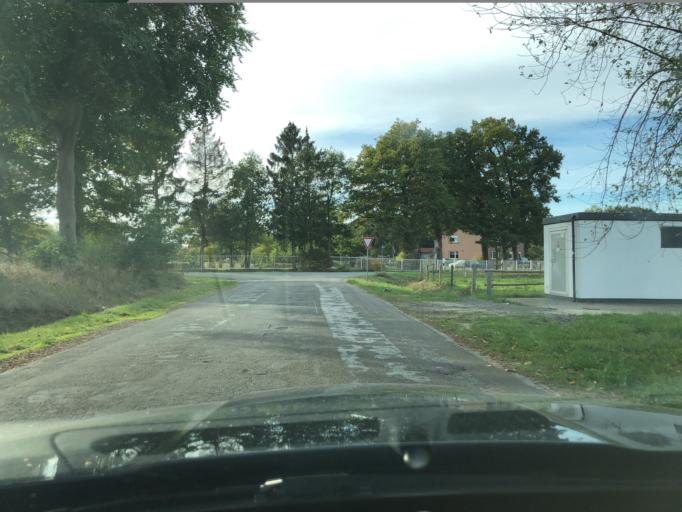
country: DE
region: North Rhine-Westphalia
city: Lengerich
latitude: 52.1692
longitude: 7.8253
